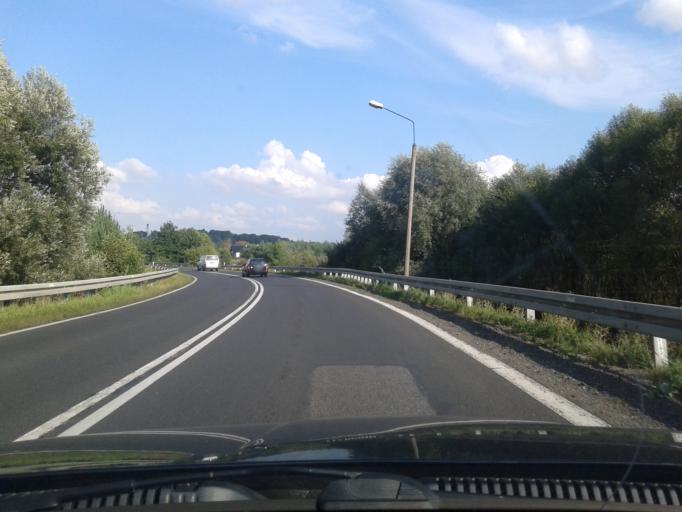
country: PL
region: Silesian Voivodeship
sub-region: Powiat wodzislawski
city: Turza Slaska
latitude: 49.9684
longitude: 18.4286
